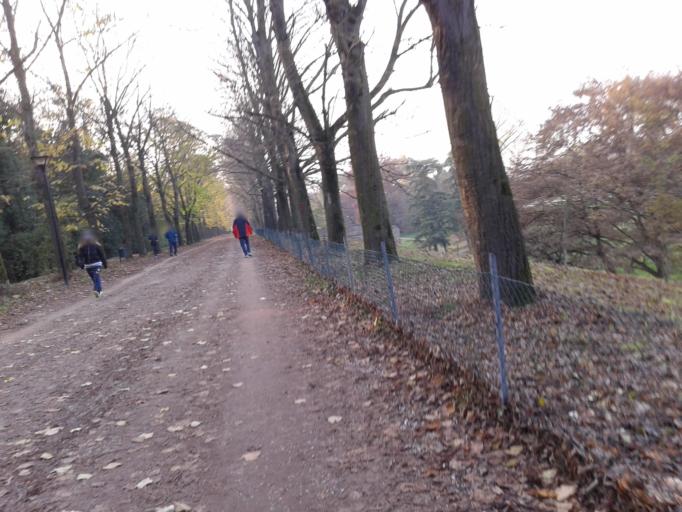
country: IT
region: Emilia-Romagna
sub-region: Provincia di Ferrara
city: Ferrara
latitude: 44.8489
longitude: 11.6282
